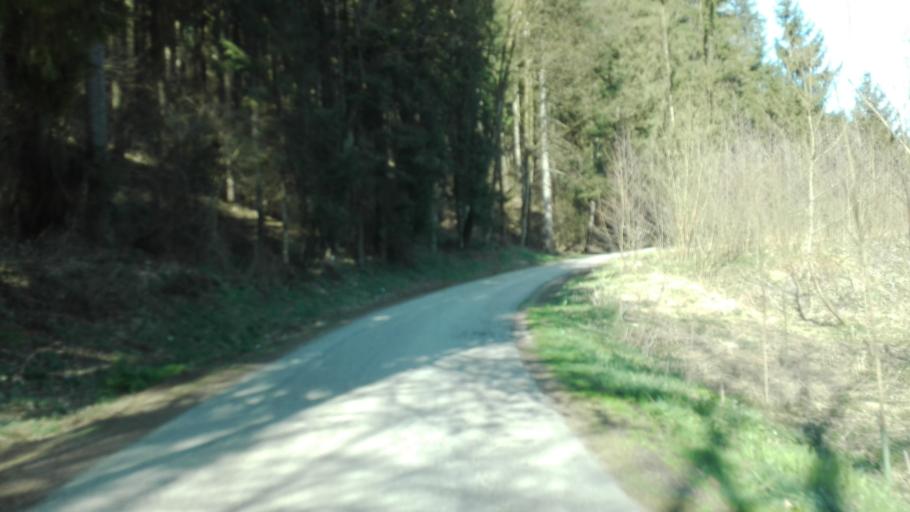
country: AT
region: Lower Austria
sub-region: Politischer Bezirk Amstetten
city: Ennsdorf
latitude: 48.2646
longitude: 14.5017
